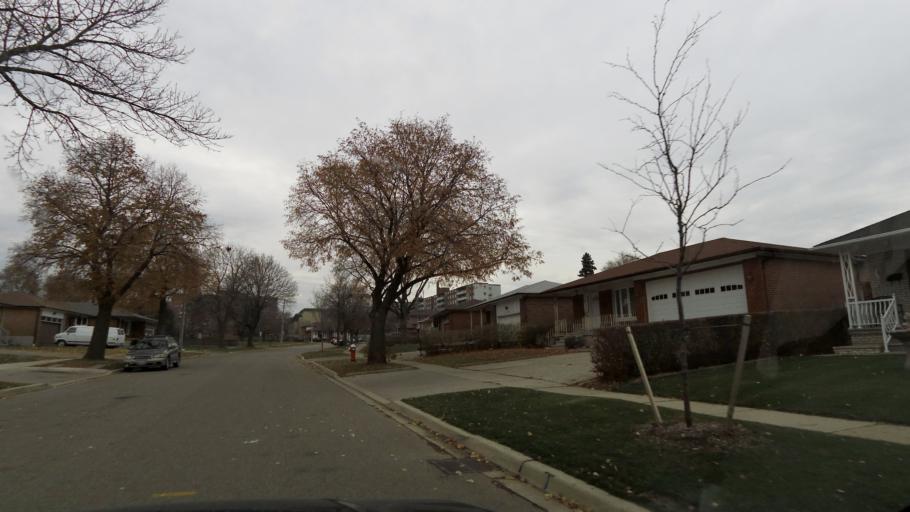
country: CA
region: Ontario
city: Etobicoke
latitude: 43.6194
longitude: -79.5864
